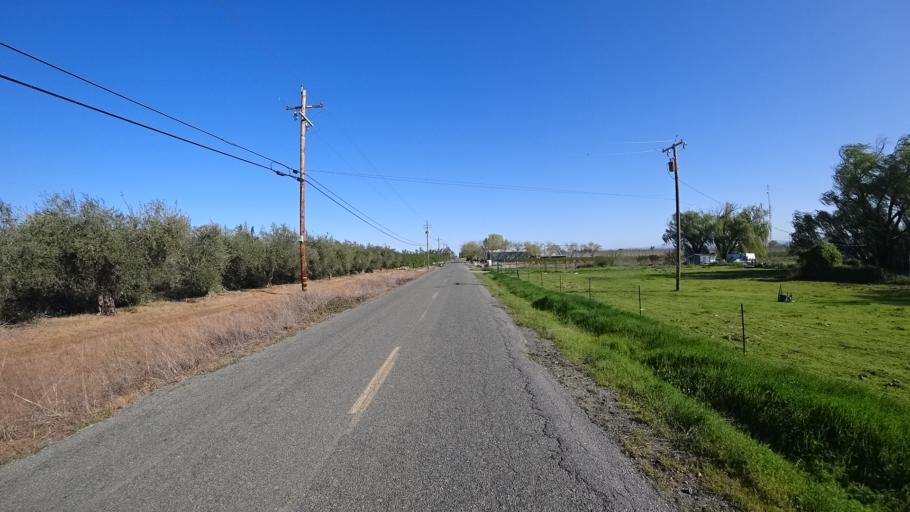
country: US
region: California
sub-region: Glenn County
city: Orland
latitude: 39.7999
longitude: -122.1040
